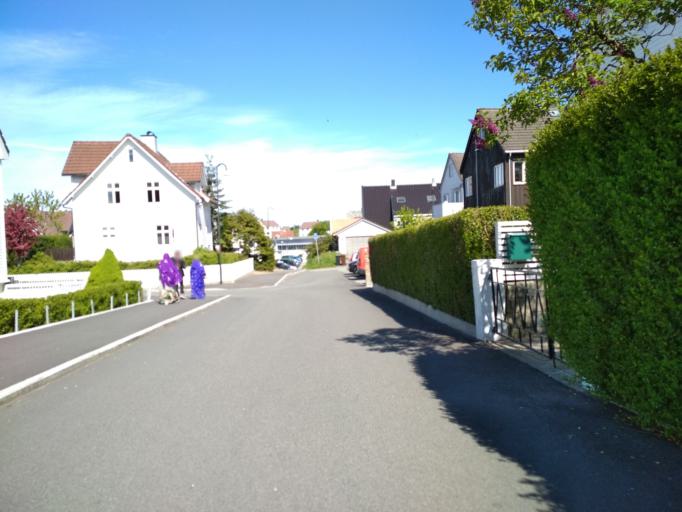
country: NO
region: Rogaland
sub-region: Stavanger
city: Stavanger
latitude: 58.9738
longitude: 5.7137
